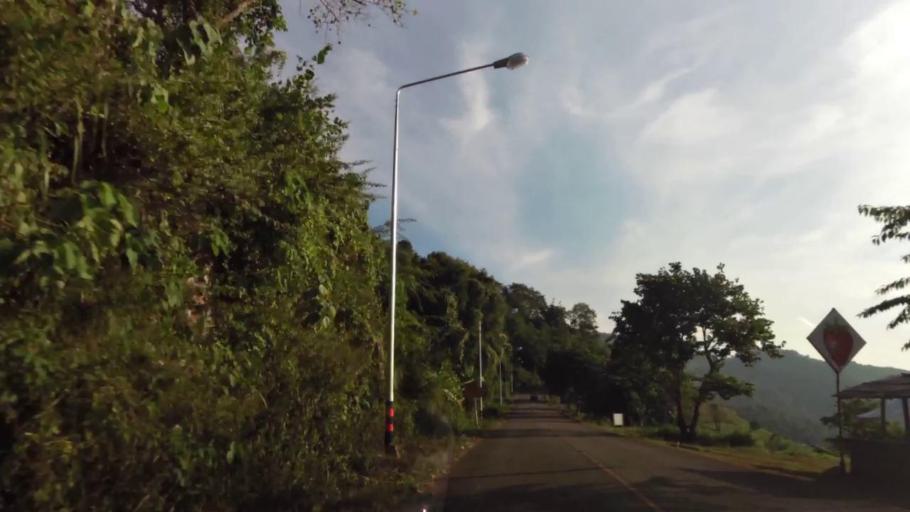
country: TH
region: Chiang Rai
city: Khun Tan
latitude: 19.8536
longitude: 100.4367
